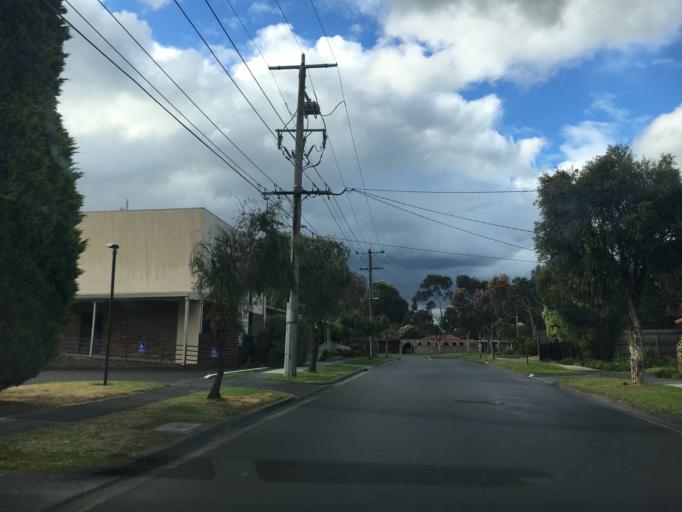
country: AU
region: Victoria
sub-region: Whitehorse
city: Vermont South
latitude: -37.8775
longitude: 145.1864
